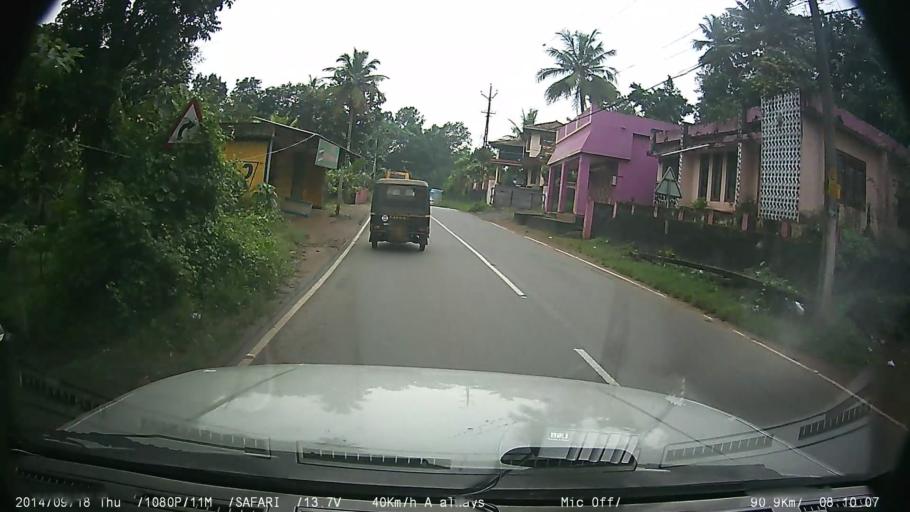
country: IN
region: Kerala
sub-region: Kottayam
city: Kottayam
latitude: 9.6020
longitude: 76.5896
